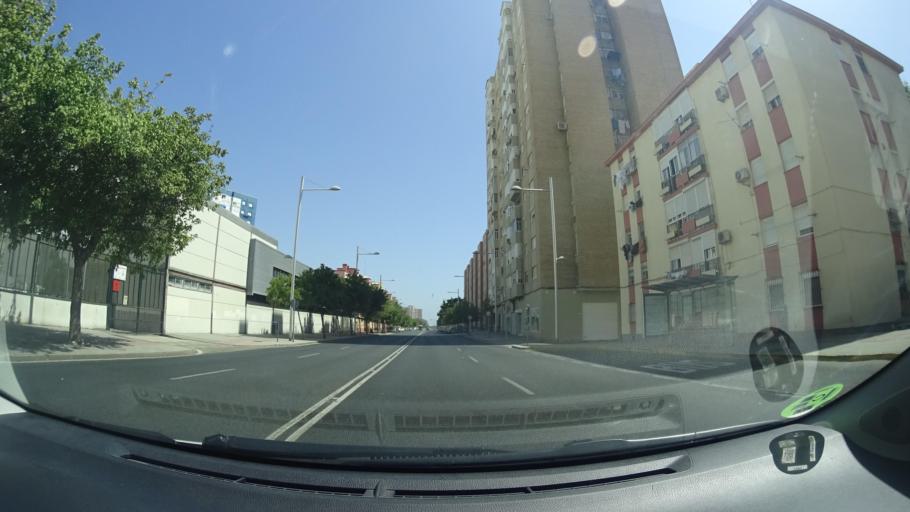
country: ES
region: Andalusia
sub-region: Provincia de Cadiz
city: Cadiz
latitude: 36.5117
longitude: -6.2761
